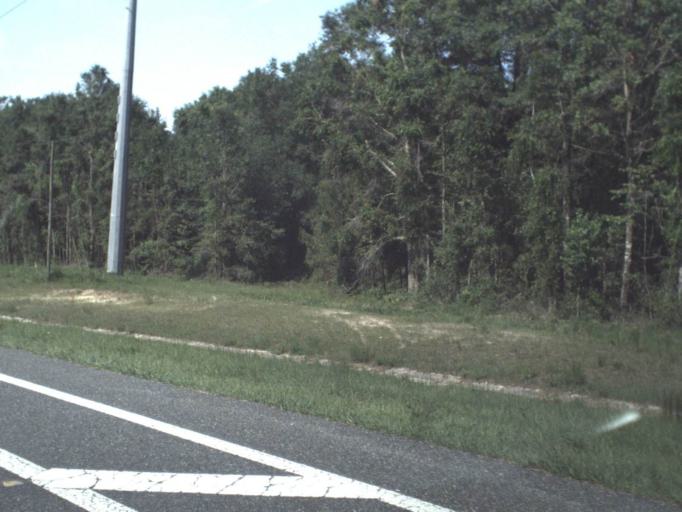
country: US
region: Florida
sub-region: Clay County
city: Middleburg
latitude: 30.0357
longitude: -81.8975
